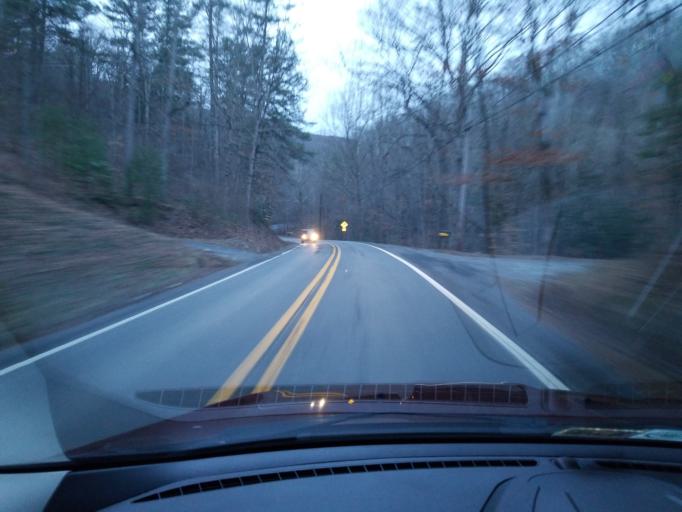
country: US
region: West Virginia
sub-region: Greenbrier County
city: Fairlea
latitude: 37.7607
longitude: -80.3973
